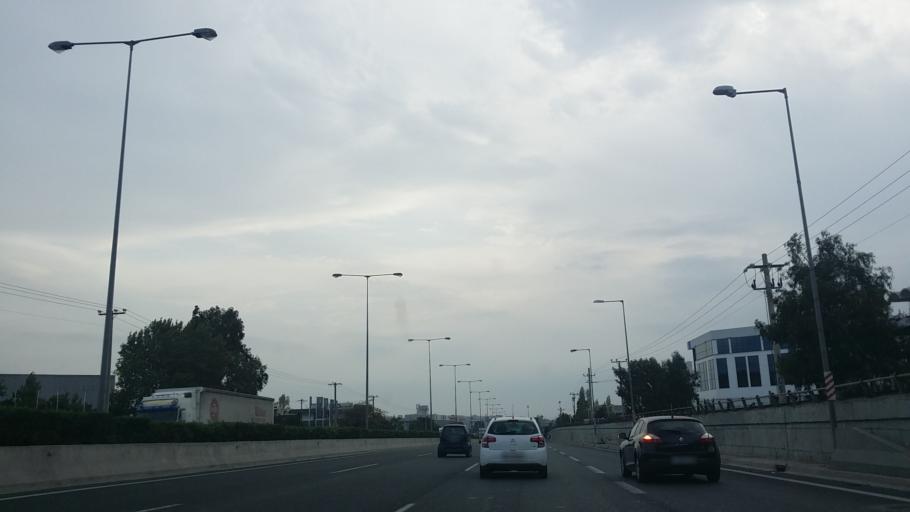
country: GR
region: Attica
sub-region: Nomarchia Athinas
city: Lykovrysi
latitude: 38.0844
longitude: 23.7855
